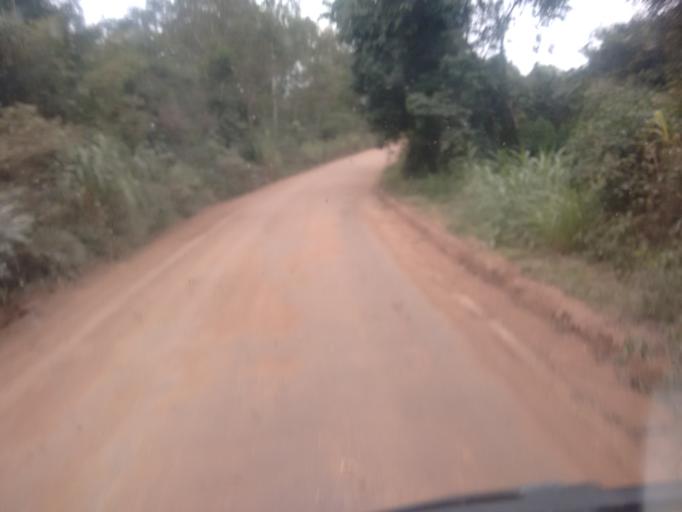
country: BR
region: Rio Grande do Sul
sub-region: Camaqua
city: Camaqua
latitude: -30.7560
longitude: -51.8810
